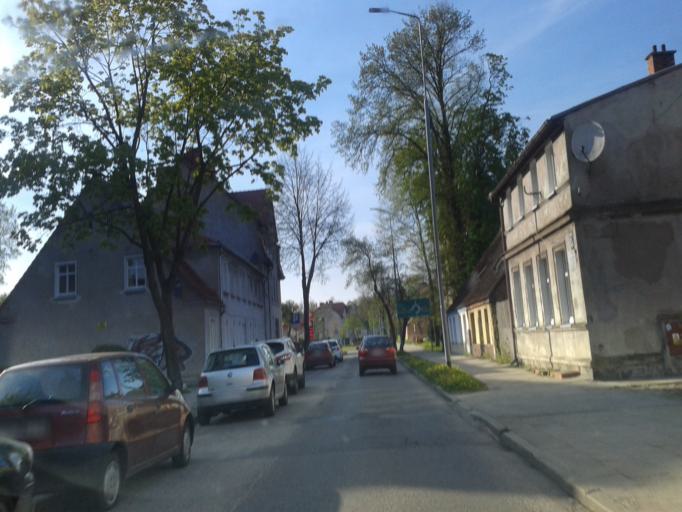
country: PL
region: West Pomeranian Voivodeship
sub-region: Powiat szczecinecki
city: Szczecinek
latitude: 53.7133
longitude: 16.6848
